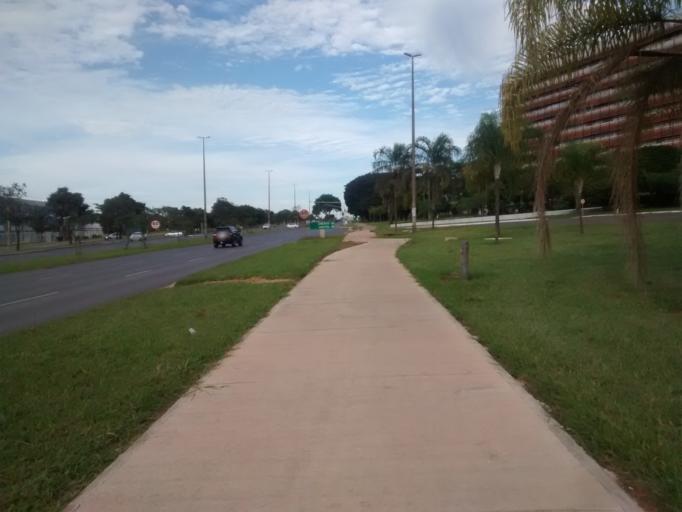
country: BR
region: Federal District
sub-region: Brasilia
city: Brasilia
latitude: -15.8053
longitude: -47.8801
